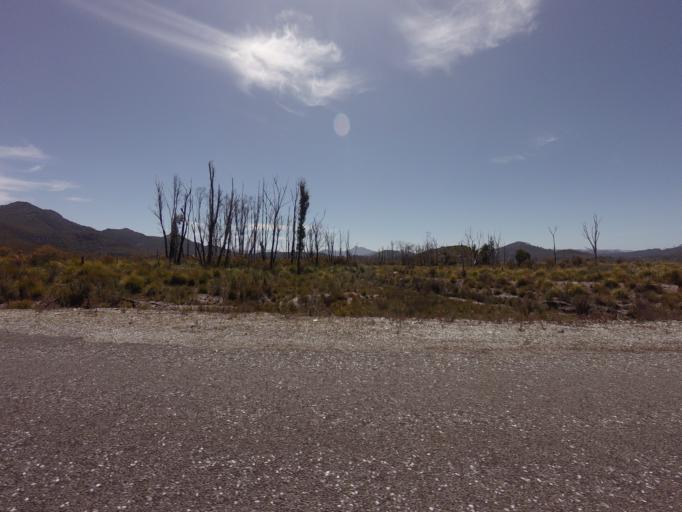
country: AU
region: Tasmania
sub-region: Huon Valley
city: Geeveston
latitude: -42.8610
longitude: 146.1990
